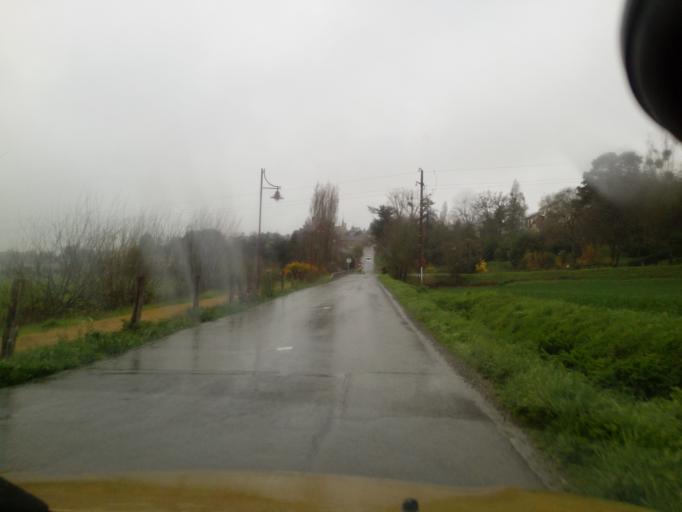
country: FR
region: Brittany
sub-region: Departement d'Ille-et-Vilaine
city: Saint-Medard-sur-Ille
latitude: 48.2466
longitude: -1.6553
